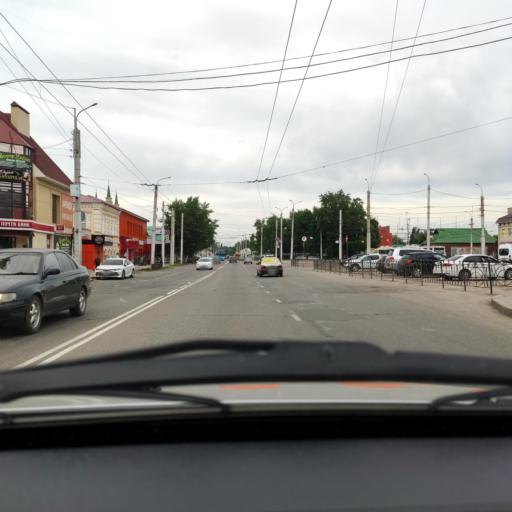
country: RU
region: Bashkortostan
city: Sterlitamak
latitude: 53.6137
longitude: 55.9554
